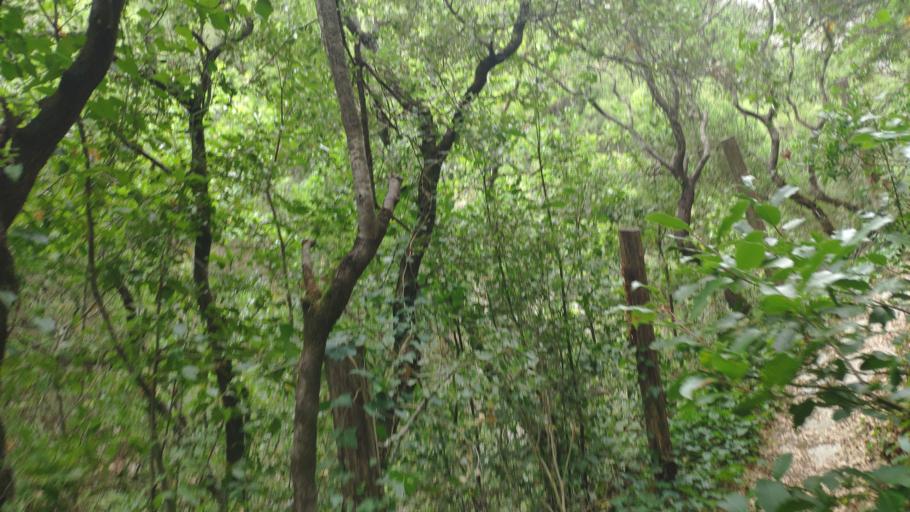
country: GR
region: Ionian Islands
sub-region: Lefkada
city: Lefkada
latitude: 38.8034
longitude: 20.6740
